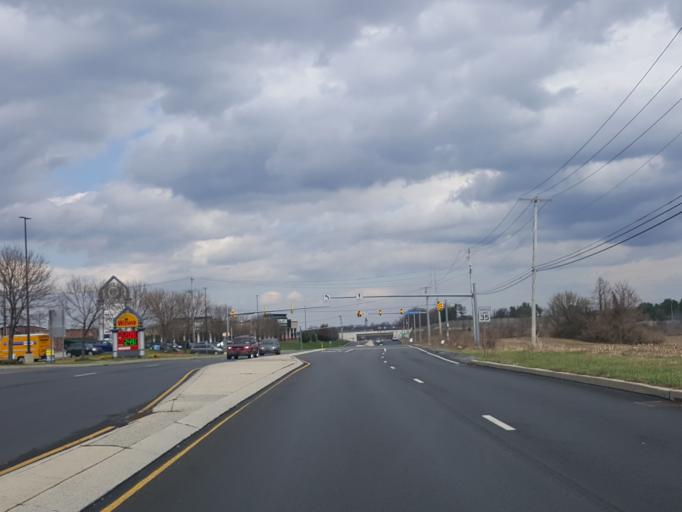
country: US
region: Pennsylvania
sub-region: Berks County
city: Spring Ridge
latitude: 40.3543
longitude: -75.9801
